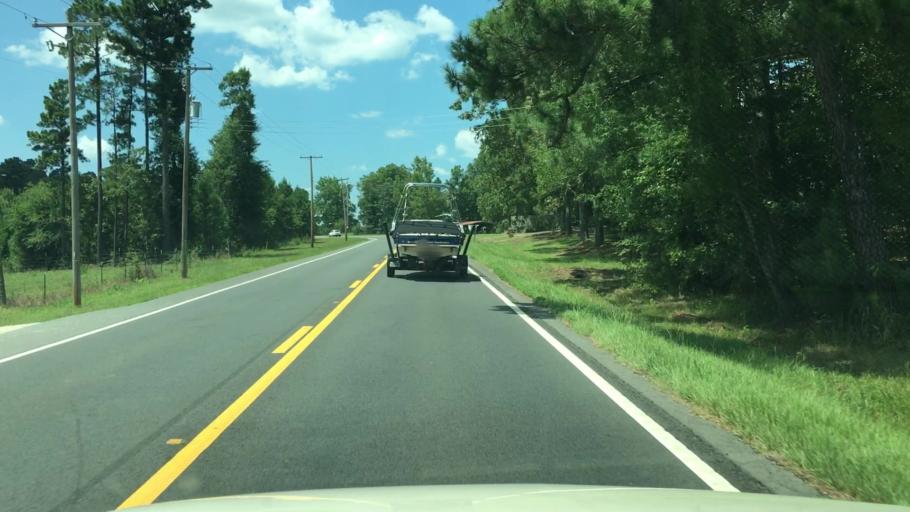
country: US
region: Arkansas
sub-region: Garland County
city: Lake Hamilton
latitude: 34.2757
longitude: -93.1503
